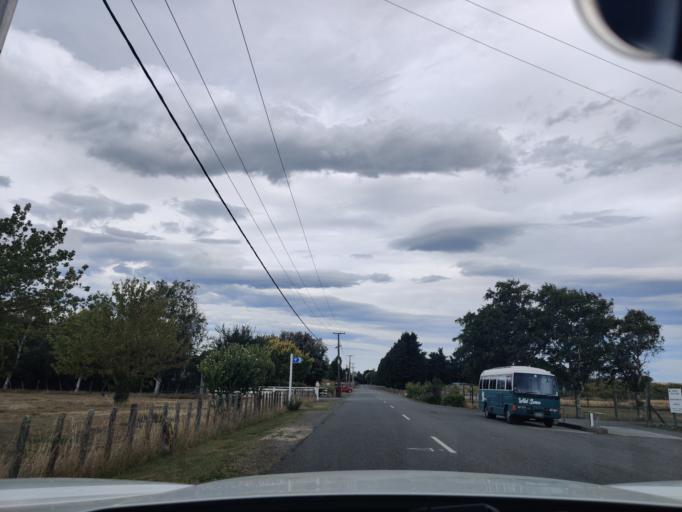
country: NZ
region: Wellington
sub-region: Masterton District
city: Masterton
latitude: -41.0400
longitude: 175.5013
